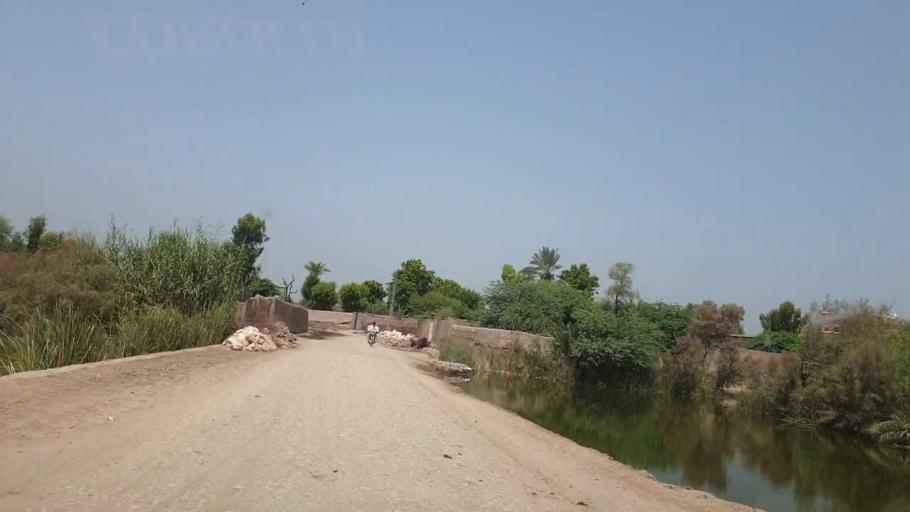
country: PK
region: Sindh
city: Shikarpur
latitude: 27.9015
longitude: 68.6624
